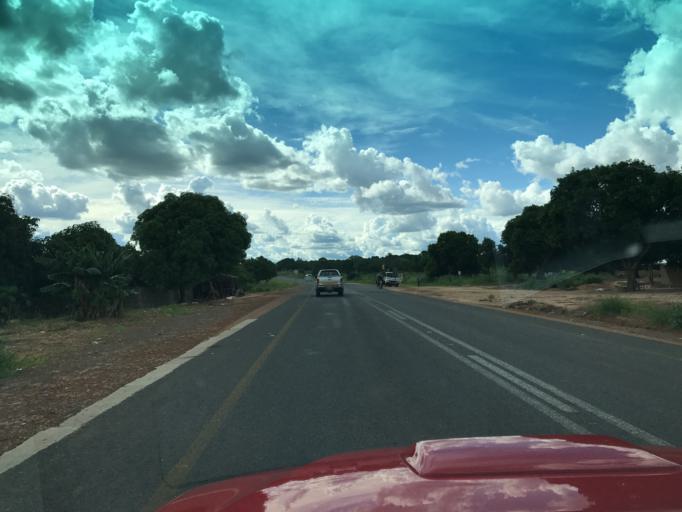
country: MZ
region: Nampula
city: Nampula
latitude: -15.0119
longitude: 39.1222
